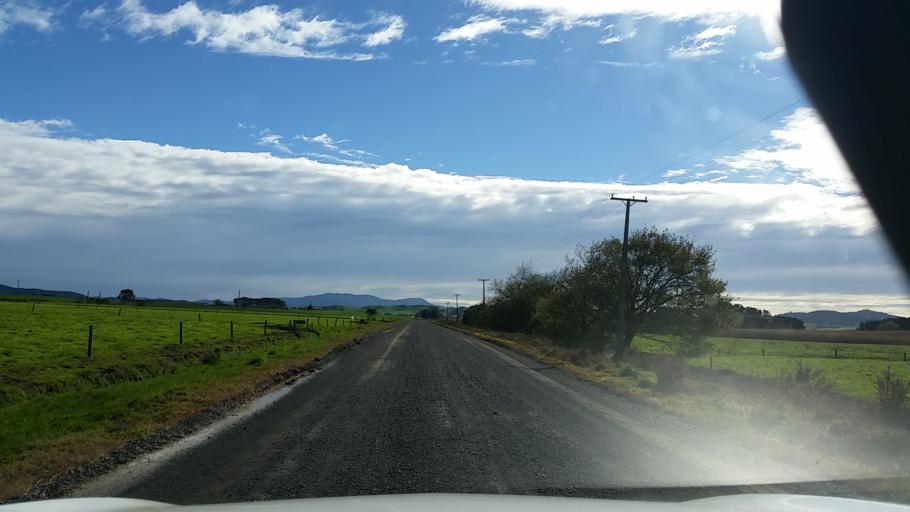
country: NZ
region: Waikato
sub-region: Hamilton City
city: Hamilton
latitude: -37.6356
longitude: 175.4297
